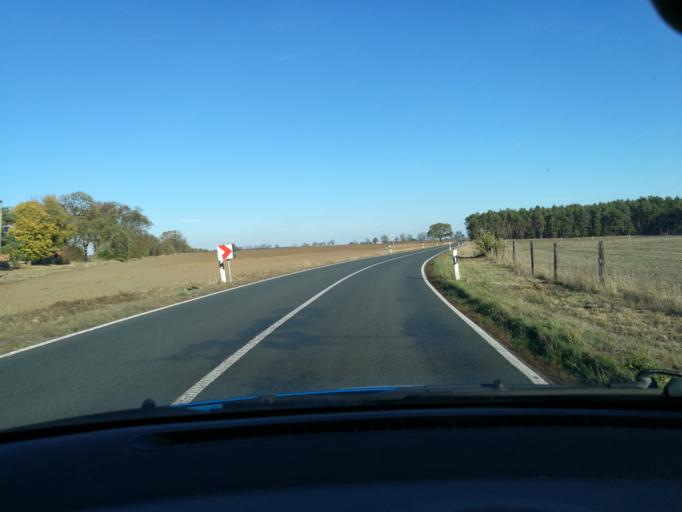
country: DE
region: Brandenburg
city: Lanz
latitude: 53.1572
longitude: 11.5944
